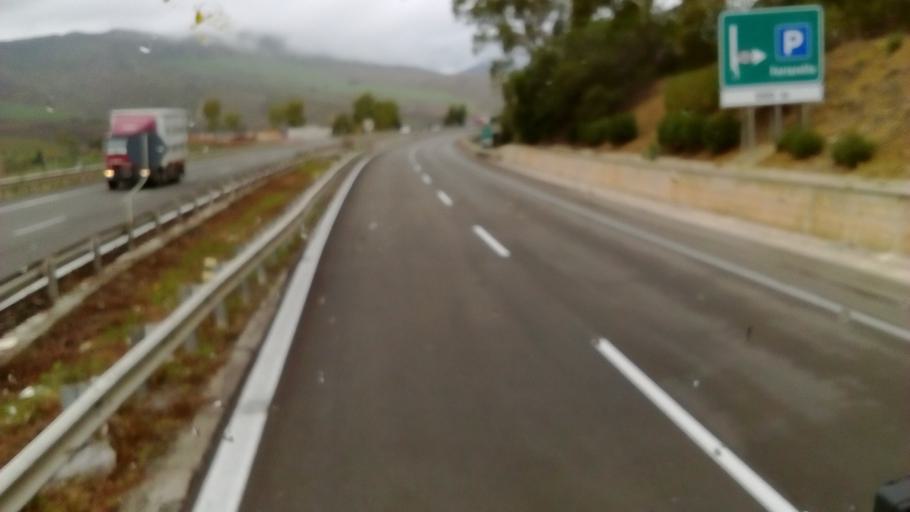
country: IT
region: Sicily
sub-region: Enna
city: Calascibetta
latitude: 37.5701
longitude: 14.2311
